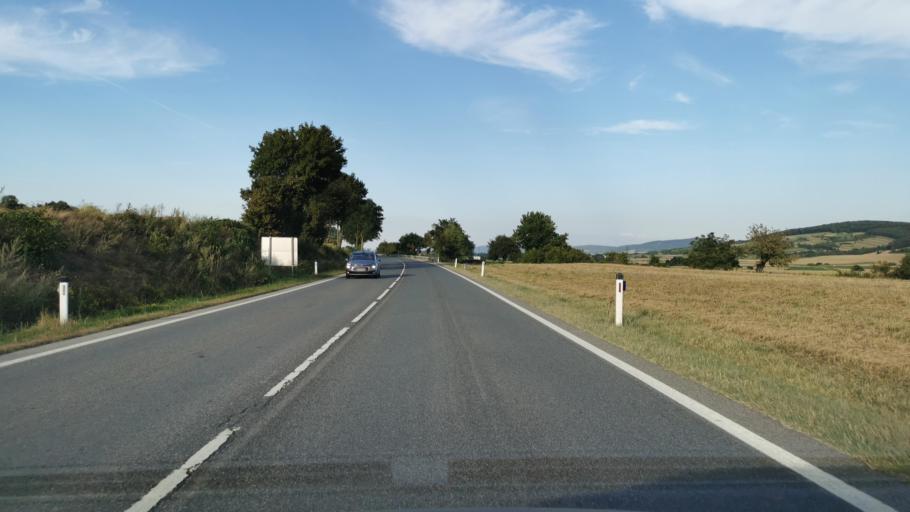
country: AT
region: Lower Austria
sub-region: Politischer Bezirk Tulln
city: Sieghartskirchen
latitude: 48.2749
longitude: 15.9890
